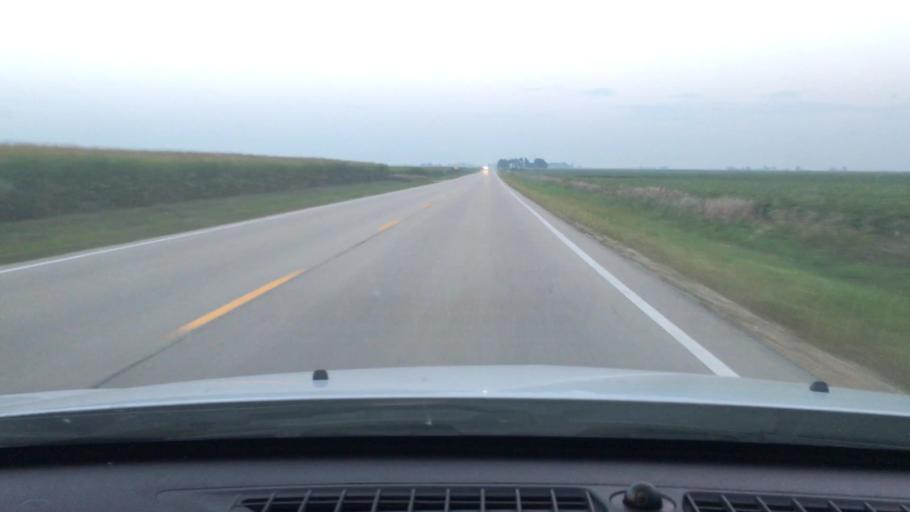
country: US
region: Illinois
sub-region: Ogle County
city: Rochelle
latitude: 41.8772
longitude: -89.0731
